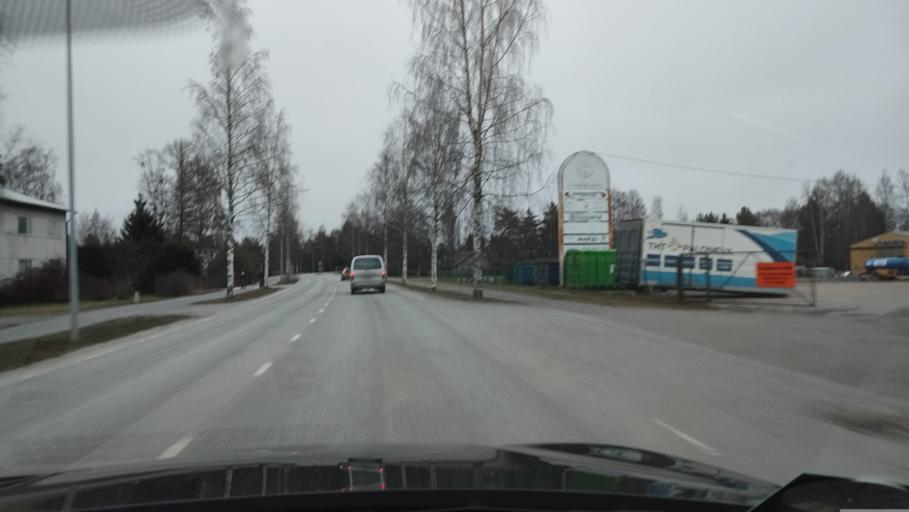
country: FI
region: Southern Ostrobothnia
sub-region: Suupohja
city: Kauhajoki
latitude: 62.4351
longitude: 22.1862
